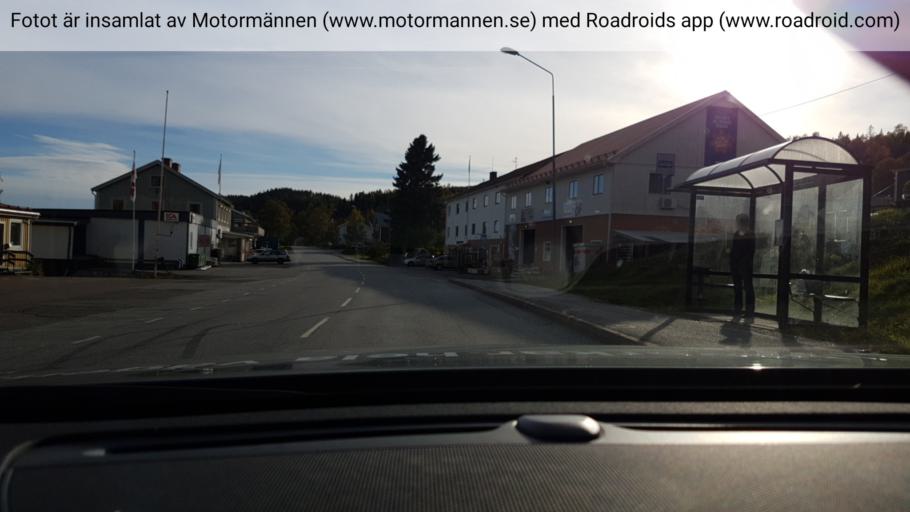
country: SE
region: Vaesternorrland
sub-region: Kramfors Kommun
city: Nordingra
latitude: 63.0556
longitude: 18.3278
